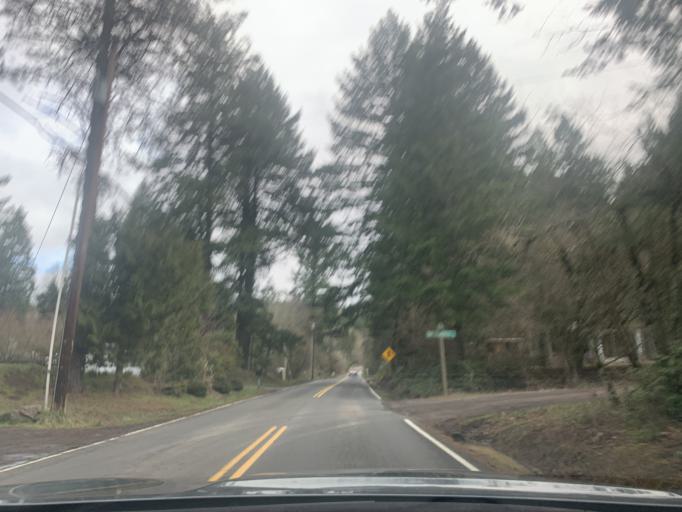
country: US
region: Oregon
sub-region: Washington County
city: Oak Hills
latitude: 45.5676
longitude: -122.8177
